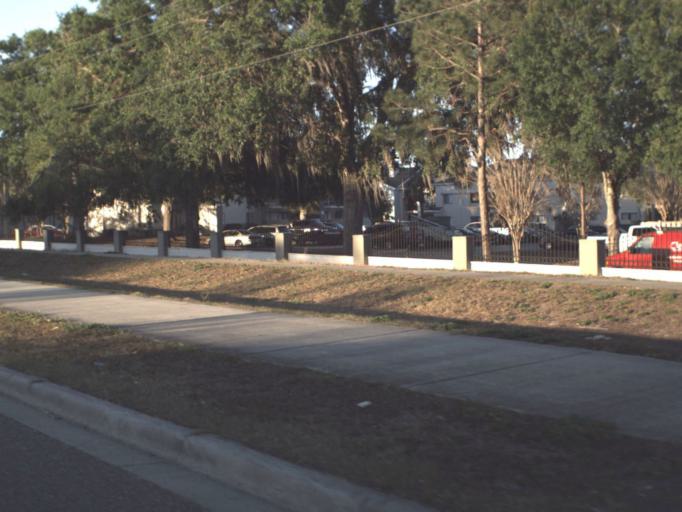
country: US
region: Florida
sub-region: Orange County
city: Conway
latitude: 28.5101
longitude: -81.3101
